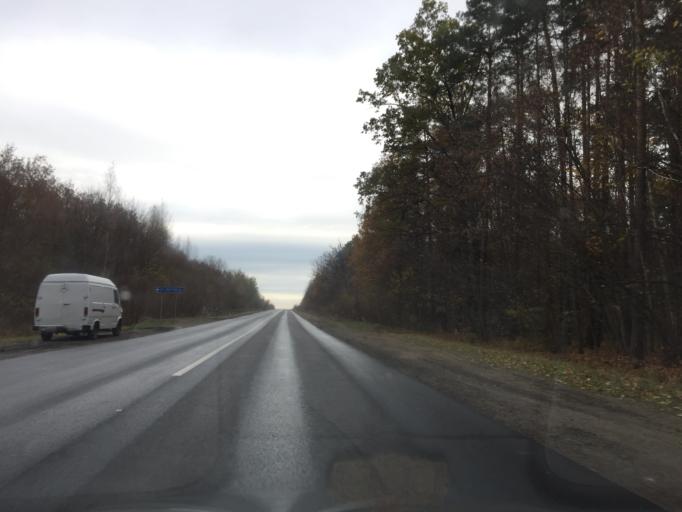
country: BY
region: Gomel
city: Gomel
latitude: 52.4108
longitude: 30.8288
